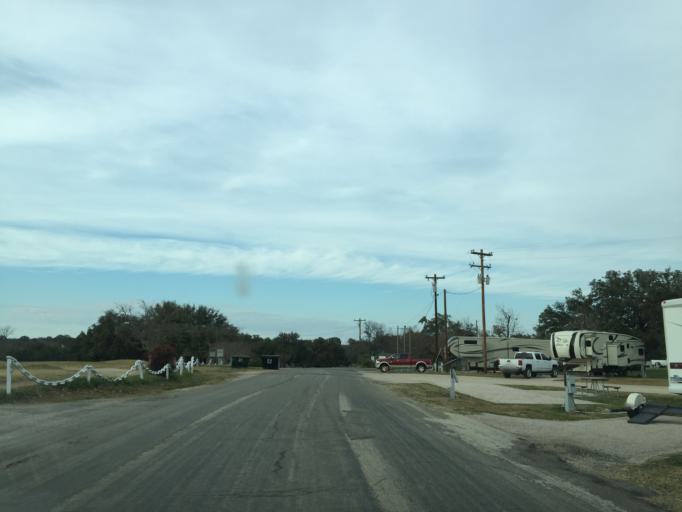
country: US
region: Texas
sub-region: Llano County
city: Llano
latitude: 30.7497
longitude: -98.7059
